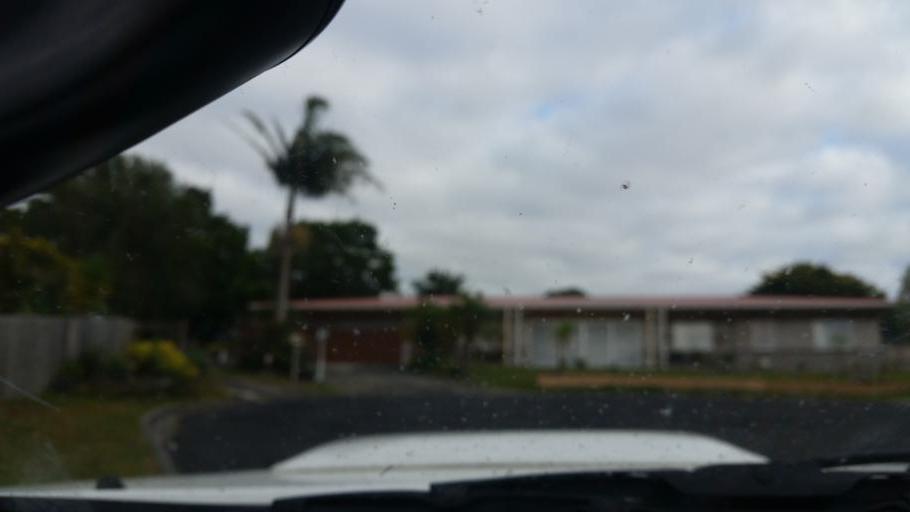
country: NZ
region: Northland
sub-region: Kaipara District
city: Dargaville
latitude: -35.9308
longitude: 173.8730
